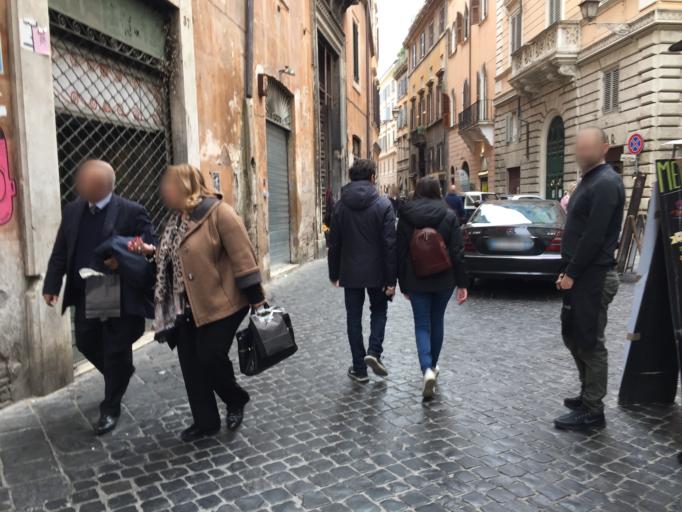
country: VA
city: Vatican City
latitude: 41.8987
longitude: 12.4698
